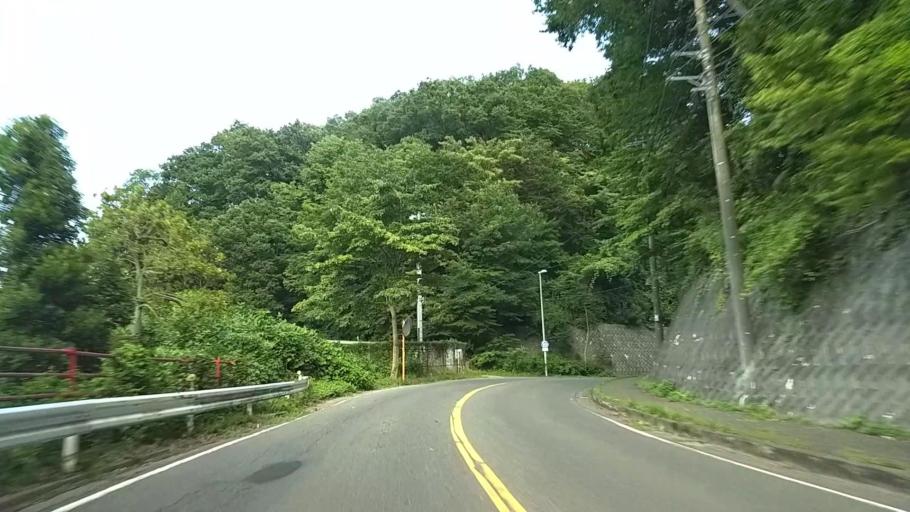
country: JP
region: Tokyo
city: Hachioji
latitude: 35.5812
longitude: 139.2610
